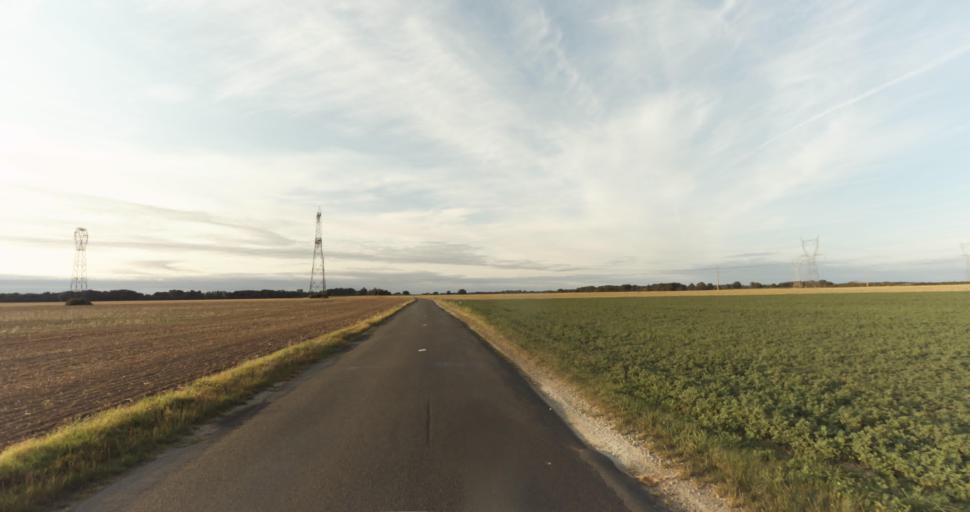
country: FR
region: Haute-Normandie
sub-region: Departement de l'Eure
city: Marcilly-sur-Eure
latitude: 48.8534
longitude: 1.2742
